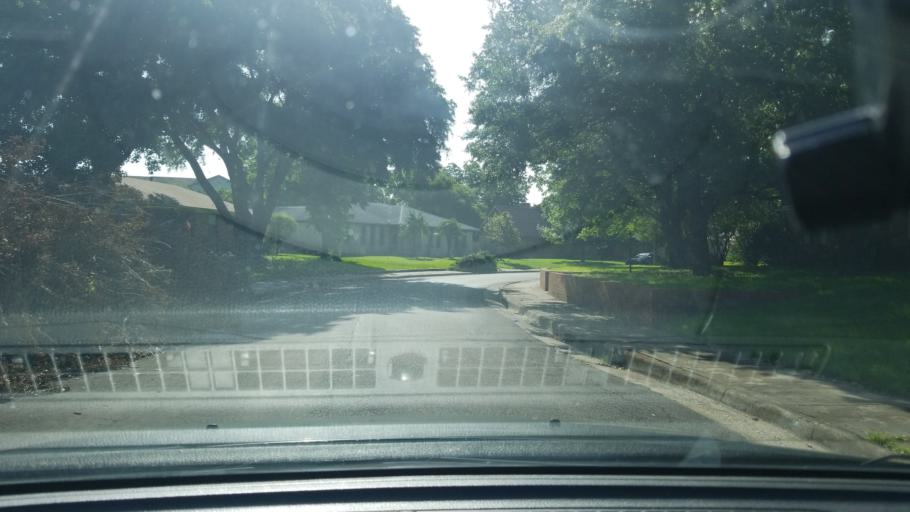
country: US
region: Texas
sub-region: Dallas County
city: Mesquite
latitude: 32.8093
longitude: -96.6750
